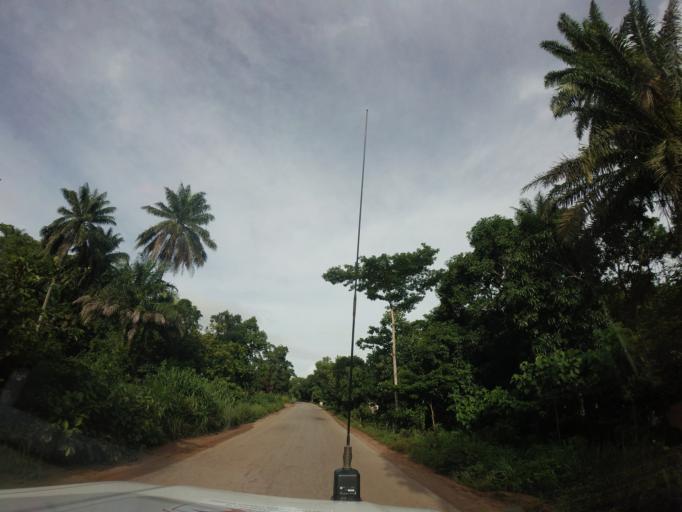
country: GN
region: Kindia
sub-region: Kindia
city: Kindia
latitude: 9.9041
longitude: -13.0167
